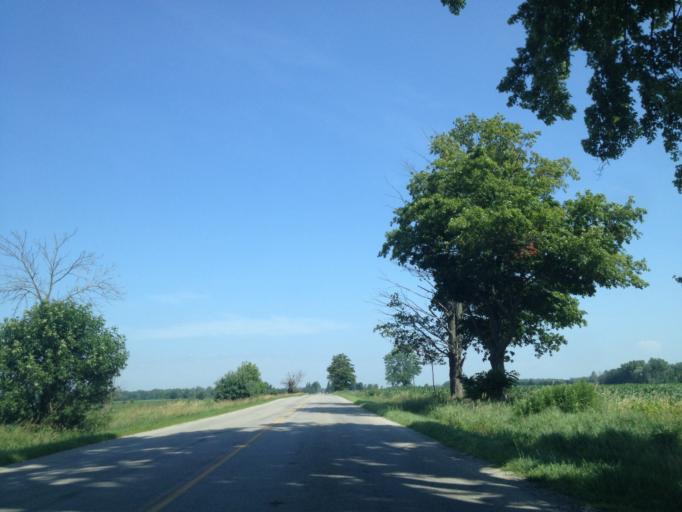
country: CA
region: Ontario
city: London
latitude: 43.1324
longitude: -81.2086
